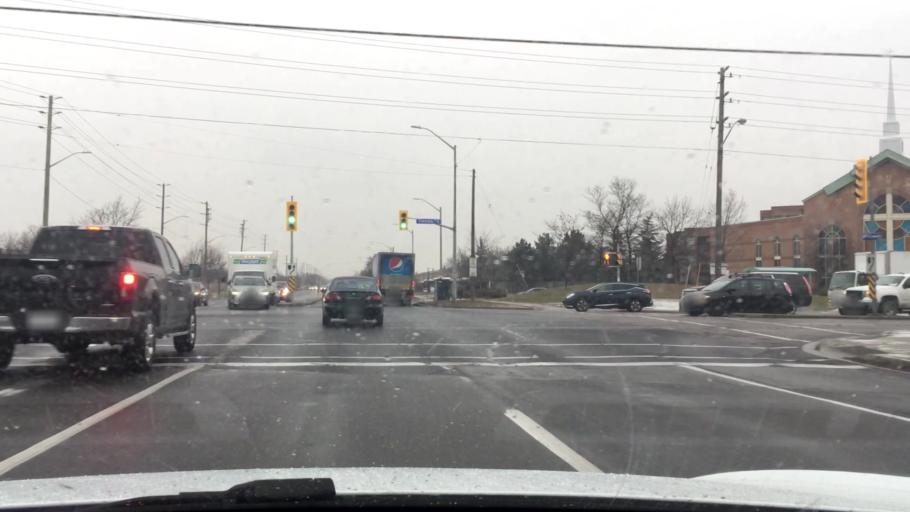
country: CA
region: Ontario
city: Markham
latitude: 43.8308
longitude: -79.2751
